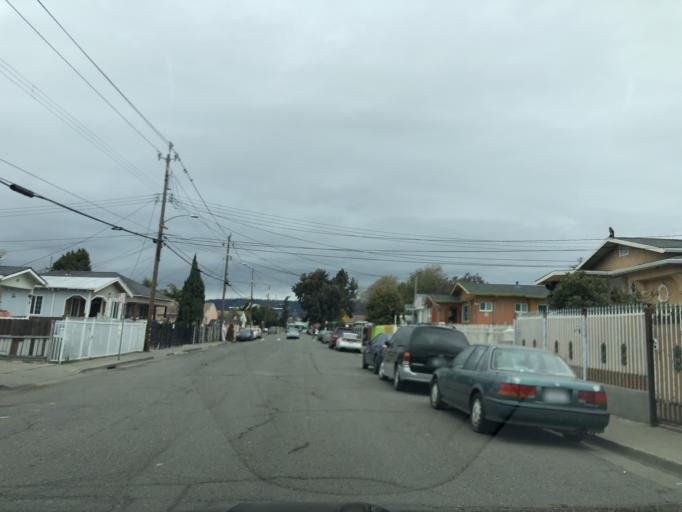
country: US
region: California
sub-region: Alameda County
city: San Leandro
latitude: 37.7312
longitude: -122.1797
